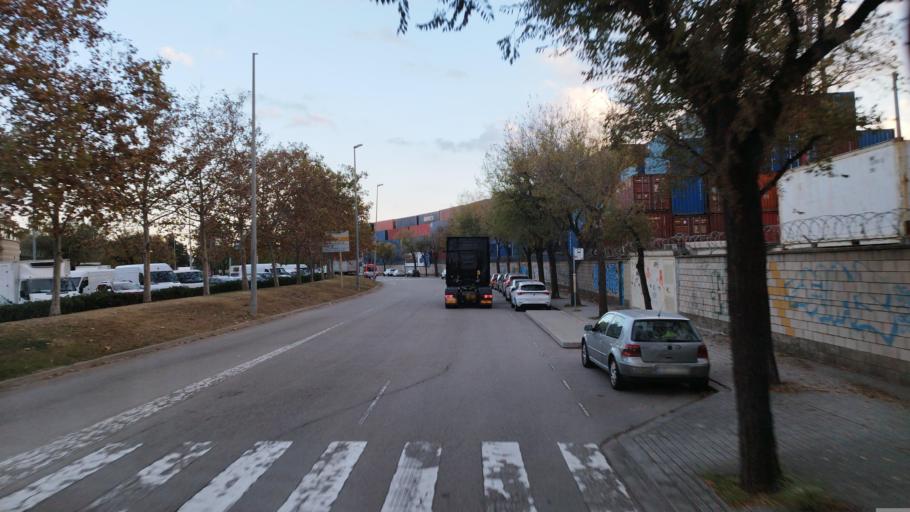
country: ES
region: Catalonia
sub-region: Provincia de Barcelona
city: L'Hospitalet de Llobregat
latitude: 41.3455
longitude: 2.1163
